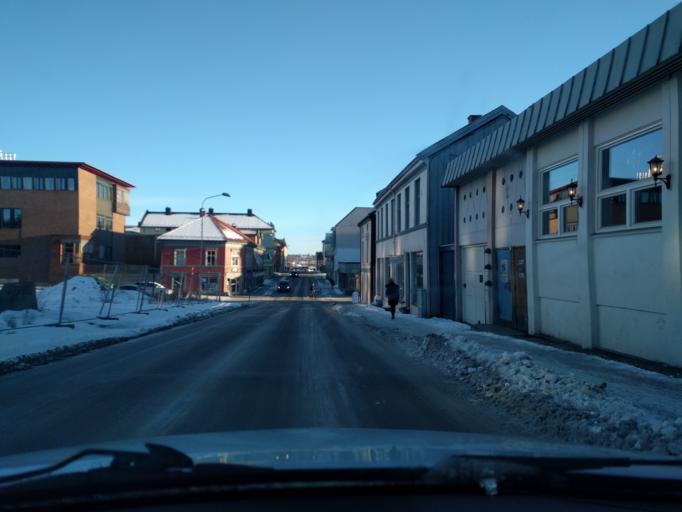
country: NO
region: Hedmark
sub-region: Hamar
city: Hamar
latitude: 60.7936
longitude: 11.0757
